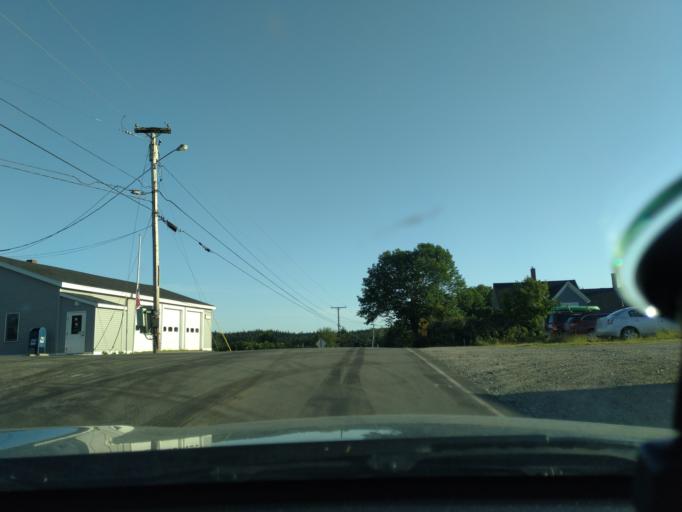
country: US
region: Maine
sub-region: Washington County
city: Machiasport
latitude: 44.6587
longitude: -67.2031
